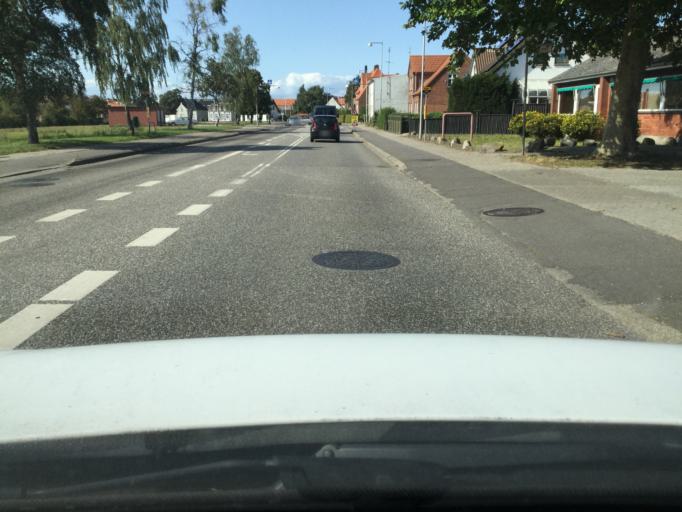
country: DK
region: Zealand
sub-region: Lolland Kommune
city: Nakskov
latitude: 54.8268
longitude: 11.1470
